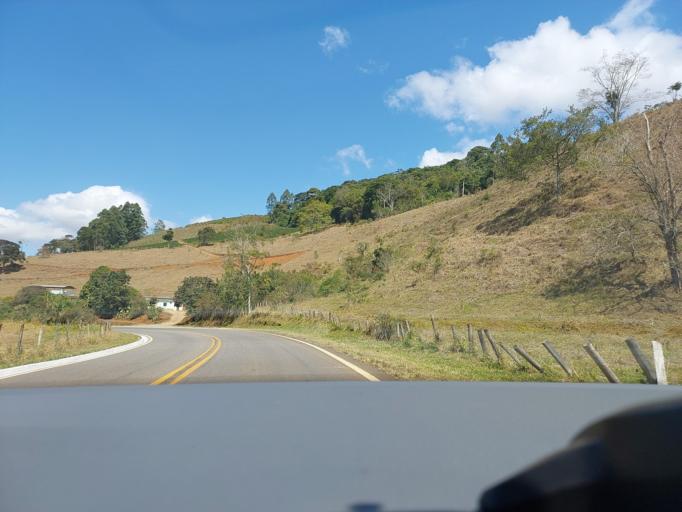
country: BR
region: Minas Gerais
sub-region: Mirai
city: Mirai
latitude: -21.0187
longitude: -42.5429
